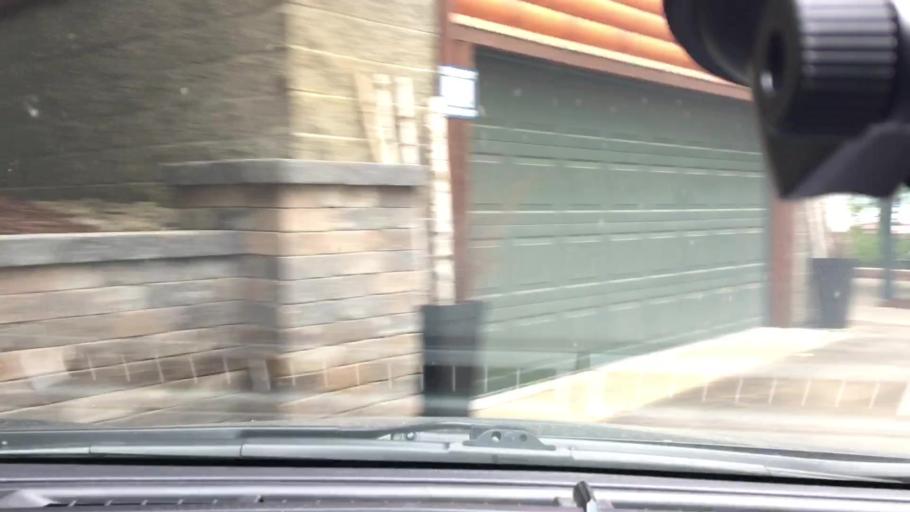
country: US
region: Minnesota
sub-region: Crow Wing County
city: Cross Lake
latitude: 46.8261
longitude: -93.9452
